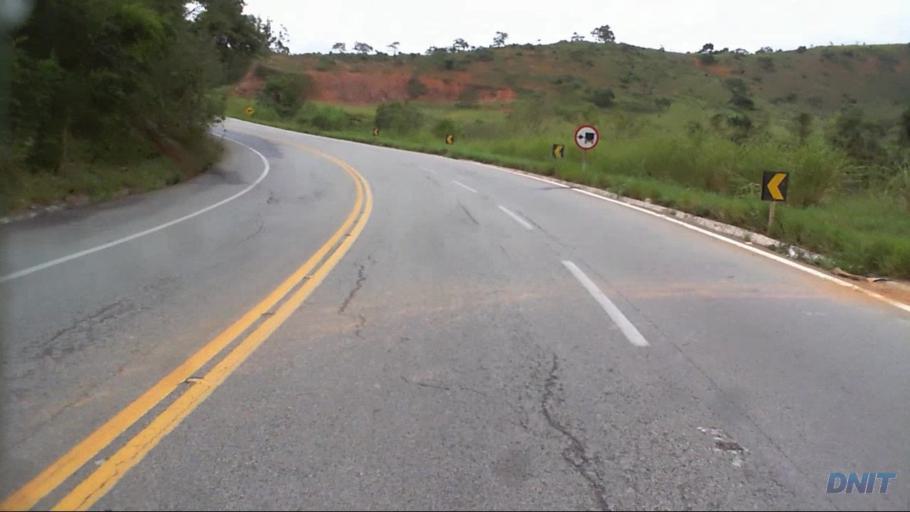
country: BR
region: Minas Gerais
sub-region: Nova Era
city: Nova Era
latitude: -19.7830
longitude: -43.0443
